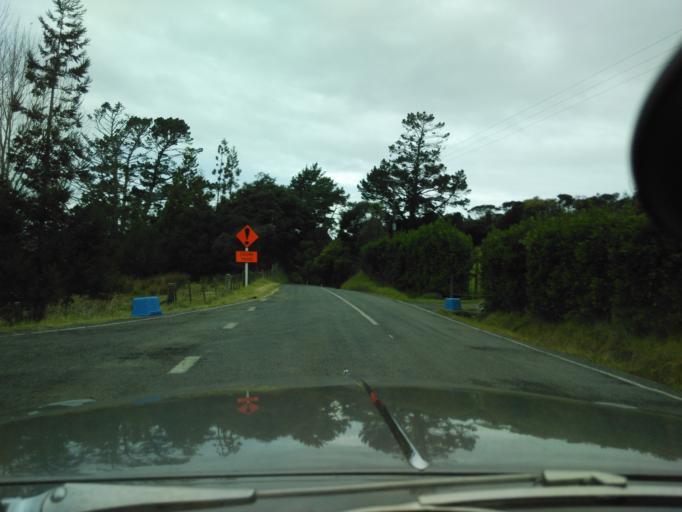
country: NZ
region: Auckland
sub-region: Auckland
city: Warkworth
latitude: -36.5315
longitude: 174.6283
